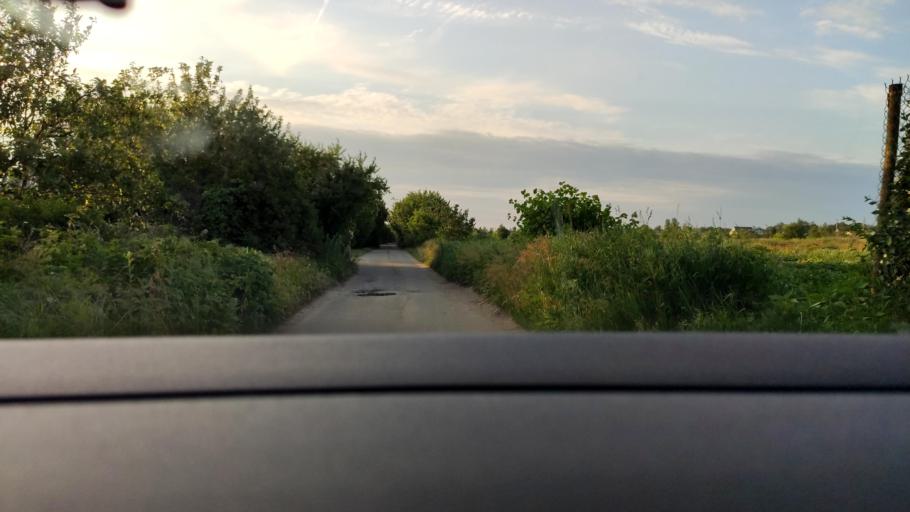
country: RU
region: Voronezj
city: Ramon'
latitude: 51.9079
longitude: 39.1771
